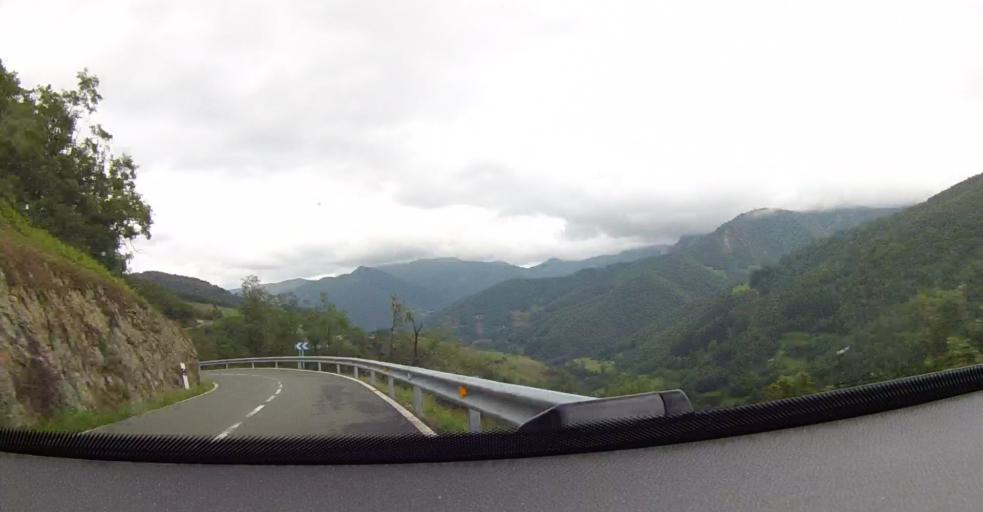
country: ES
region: Cantabria
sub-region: Provincia de Cantabria
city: Camaleno
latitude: 43.0936
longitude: -4.6976
